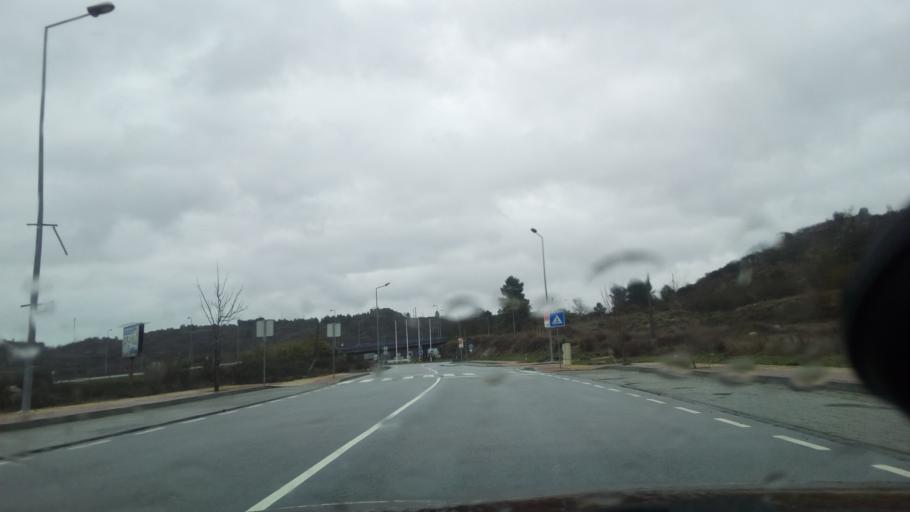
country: PT
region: Guarda
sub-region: Celorico da Beira
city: Celorico da Beira
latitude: 40.6287
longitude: -7.4162
